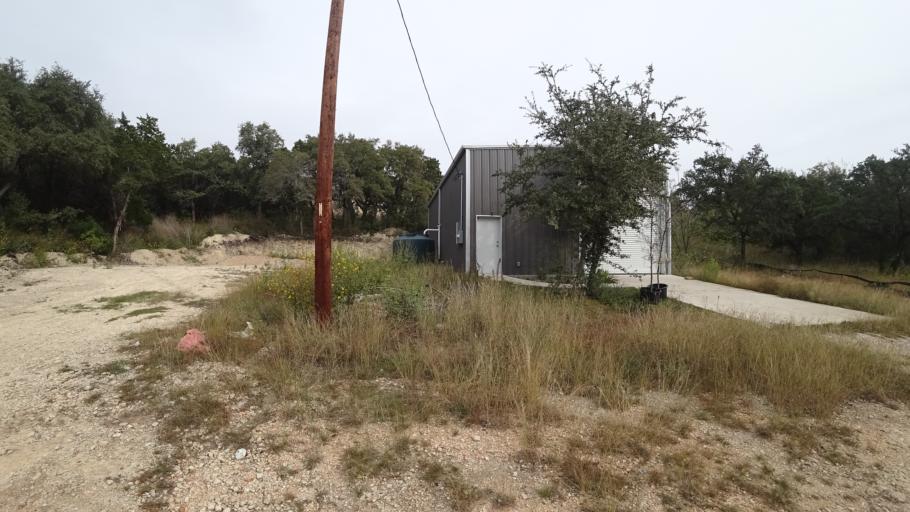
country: US
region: Texas
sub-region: Travis County
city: Hudson Bend
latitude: 30.3958
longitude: -97.9243
